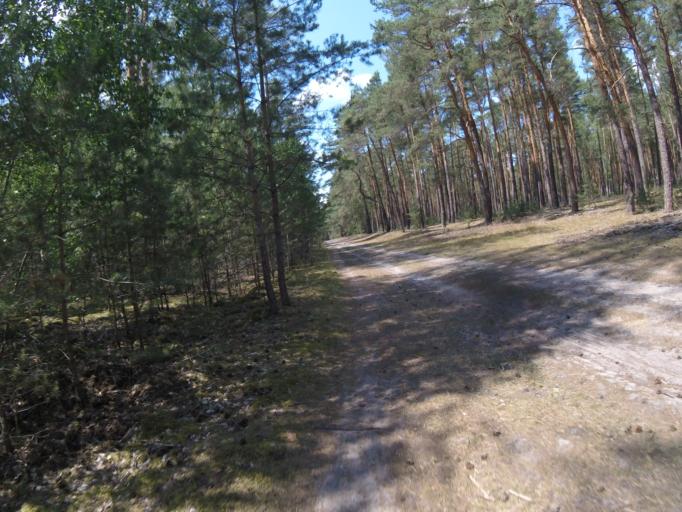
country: DE
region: Brandenburg
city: Bestensee
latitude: 52.2521
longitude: 13.6784
